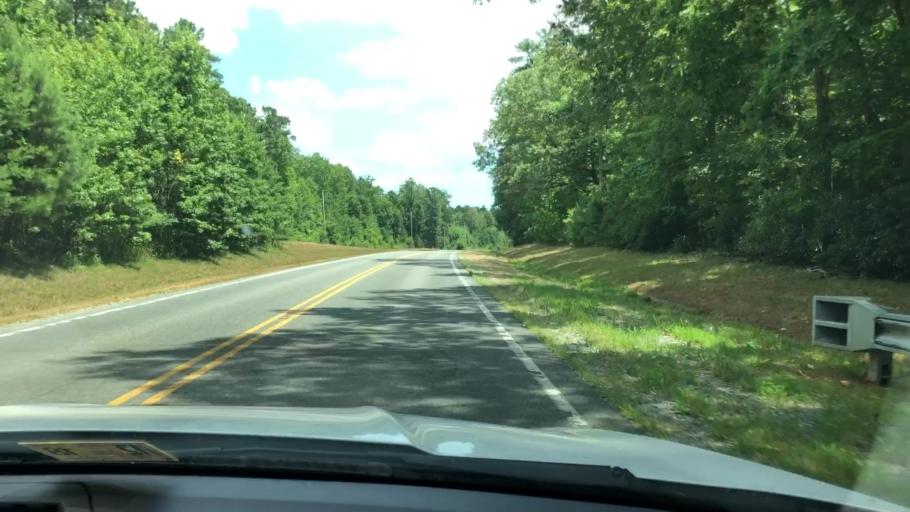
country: US
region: Virginia
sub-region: Lancaster County
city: Lancaster
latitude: 37.8257
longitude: -76.5611
